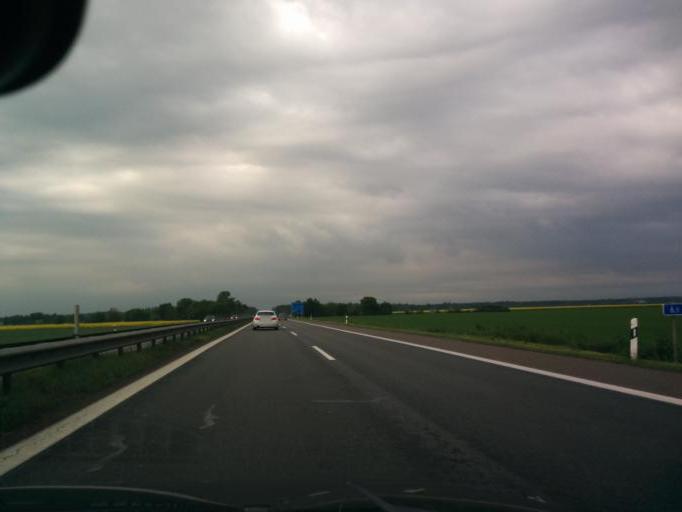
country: DE
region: Bavaria
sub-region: Upper Bavaria
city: Ottobrunn
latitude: 48.0518
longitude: 11.6453
